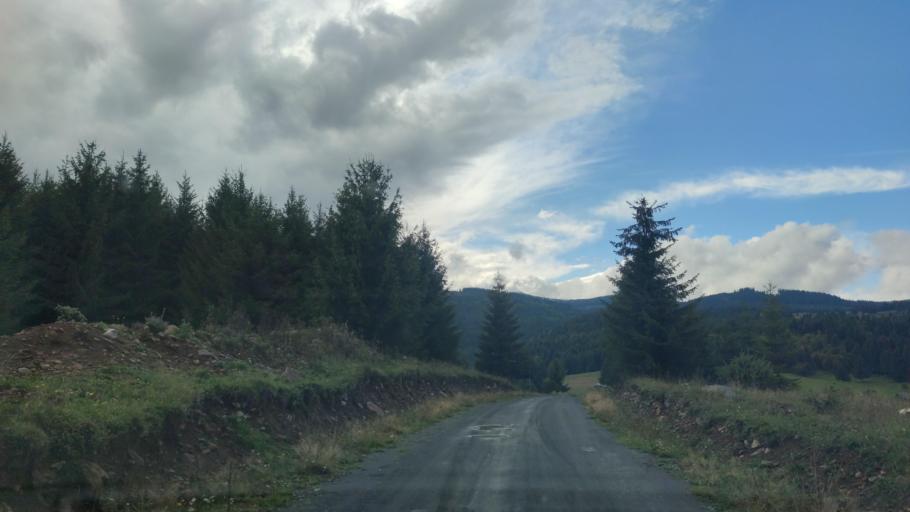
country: RO
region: Harghita
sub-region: Comuna Remetea
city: Remetea
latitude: 46.8151
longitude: 25.3616
